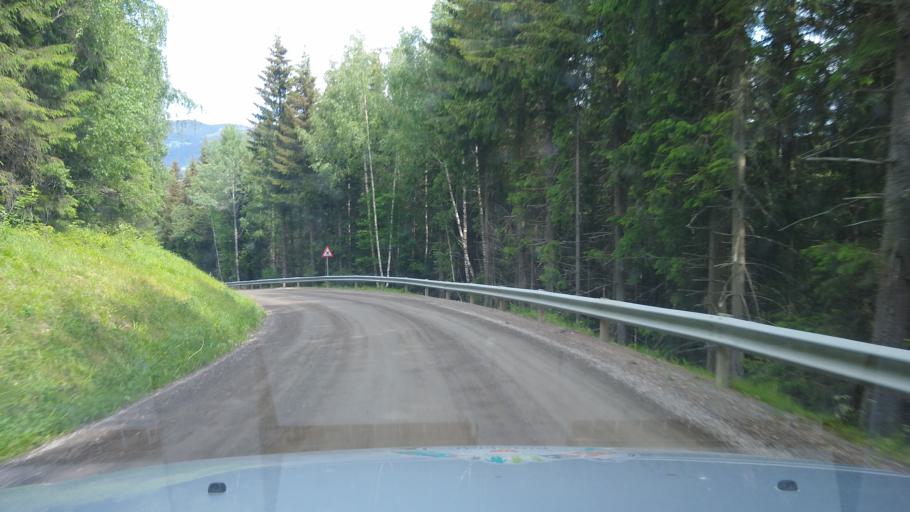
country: NO
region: Oppland
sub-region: Ringebu
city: Ringebu
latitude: 61.5191
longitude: 10.1310
